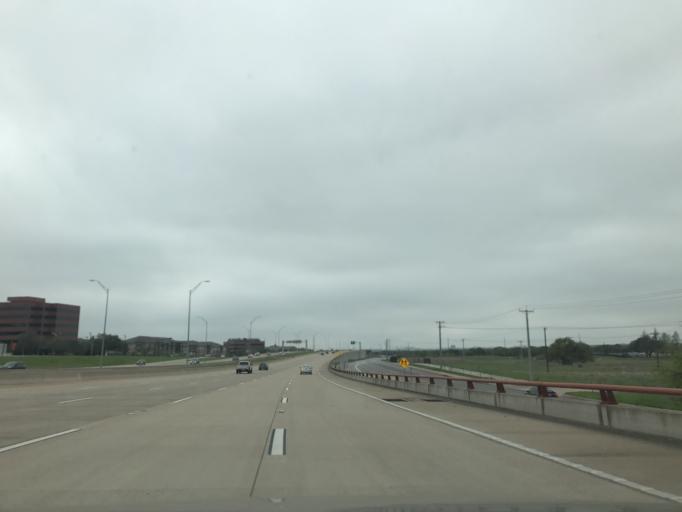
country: US
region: Texas
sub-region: Travis County
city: Wells Branch
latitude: 30.4466
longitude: -97.6968
